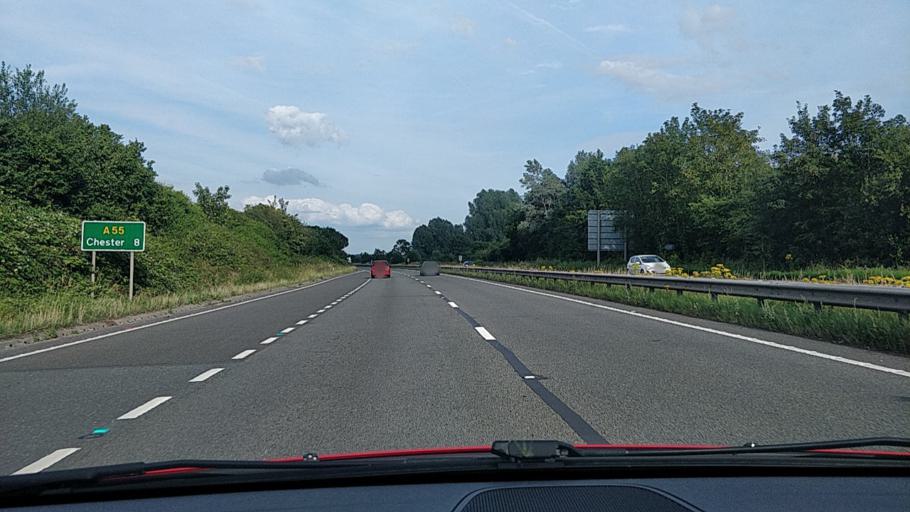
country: GB
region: Wales
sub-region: County of Flintshire
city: Hawarden
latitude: 53.1604
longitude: -3.0016
